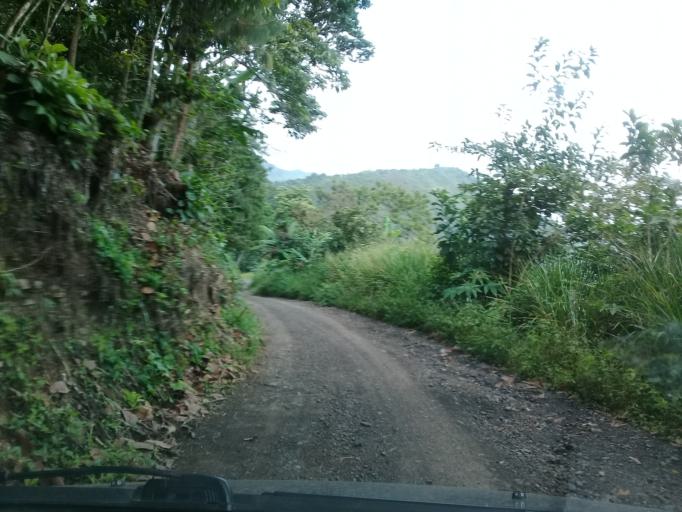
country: CO
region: Cundinamarca
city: Viani
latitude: 4.8513
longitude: -74.5496
